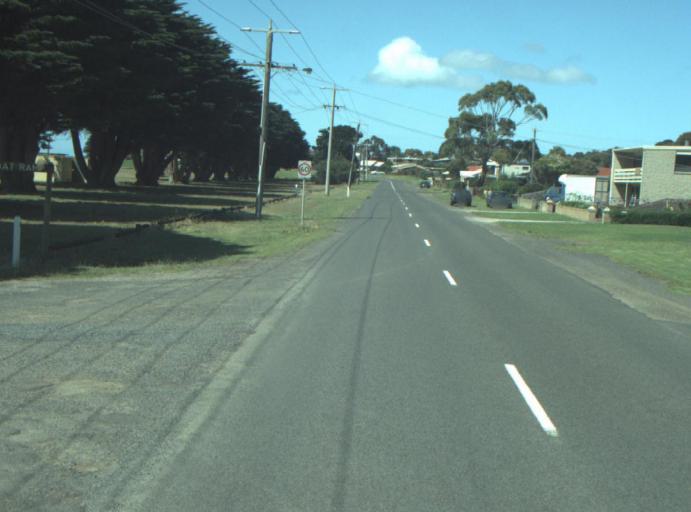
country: AU
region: Victoria
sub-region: Queenscliffe
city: Queenscliff
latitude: -38.1801
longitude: 144.7150
